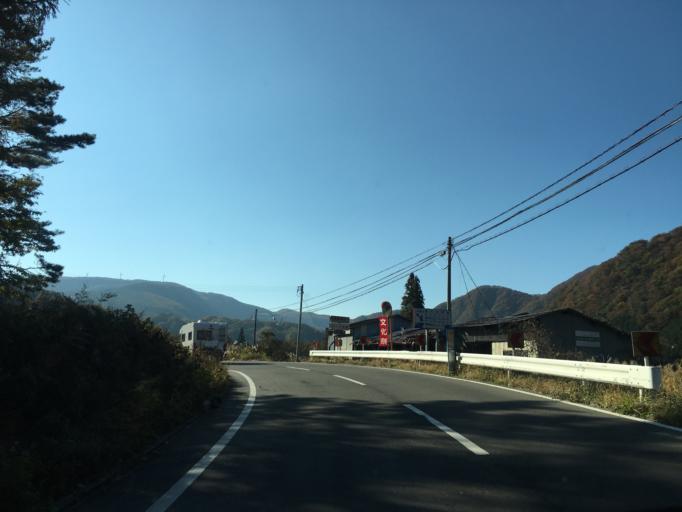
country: JP
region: Fukushima
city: Inawashiro
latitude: 37.2806
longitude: 140.0047
